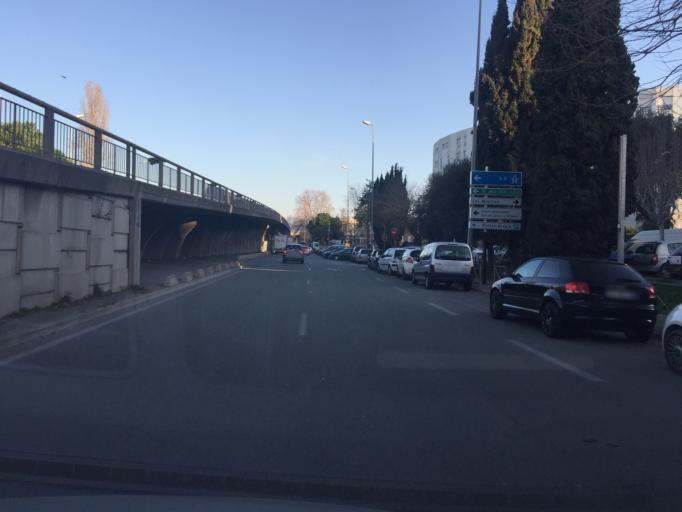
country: FR
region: Provence-Alpes-Cote d'Azur
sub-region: Departement des Alpes-Maritimes
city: Saint-Laurent-du-Var
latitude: 43.6754
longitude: 7.2017
